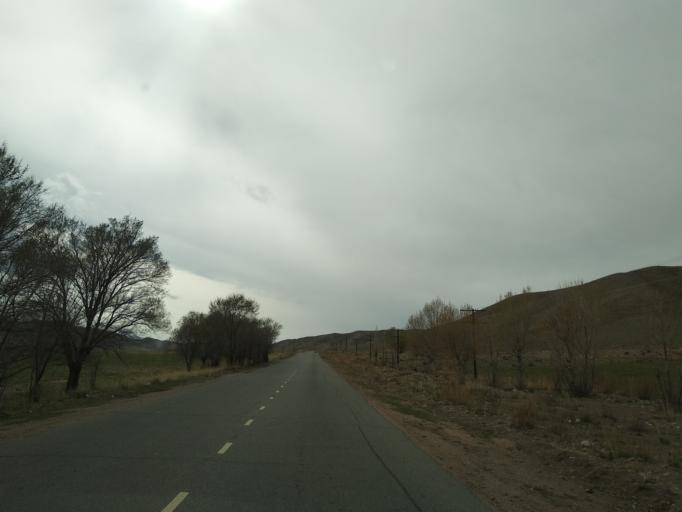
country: KG
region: Ysyk-Koel
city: Bokombayevskoye
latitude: 42.1326
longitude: 76.7947
